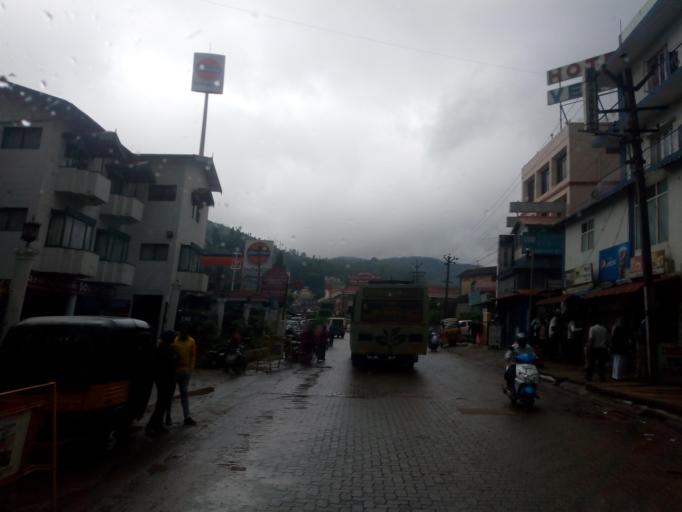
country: IN
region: Tamil Nadu
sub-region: Nilgiri
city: Ooty
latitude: 11.4107
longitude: 76.7109
